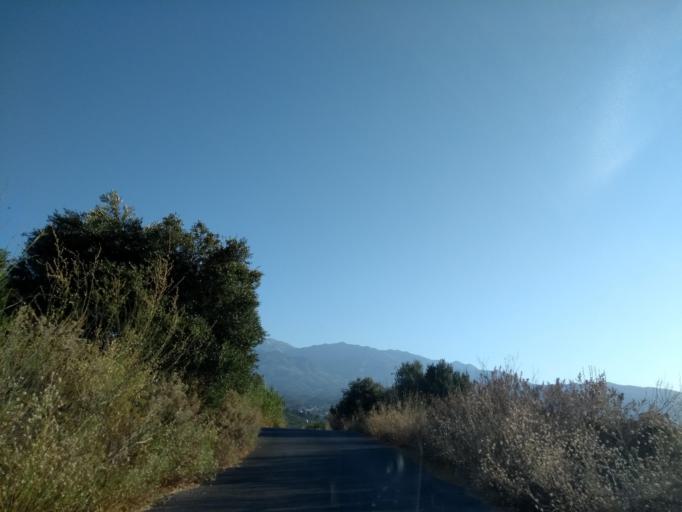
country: GR
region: Crete
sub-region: Nomos Chanias
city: Kalivai
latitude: 35.4456
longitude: 24.1729
